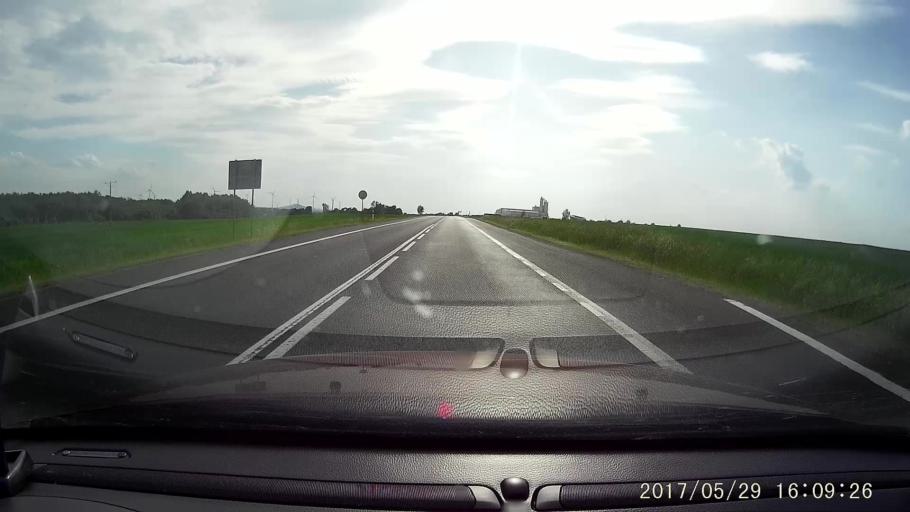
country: PL
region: Lower Silesian Voivodeship
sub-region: Powiat zgorzelecki
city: Piensk
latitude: 51.2050
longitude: 15.1153
